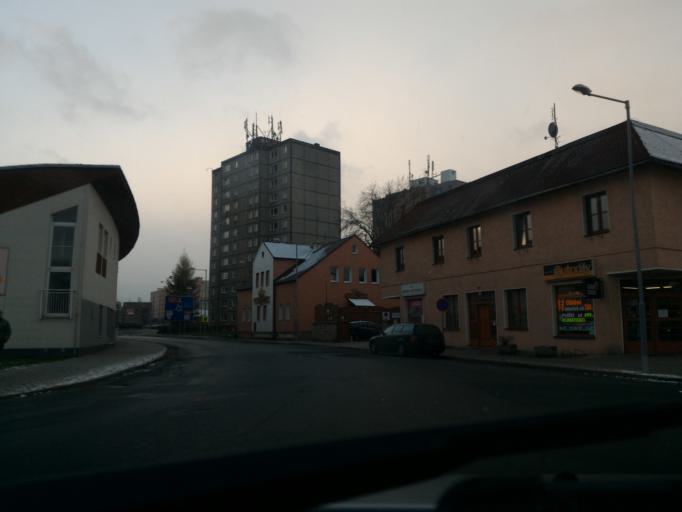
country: CZ
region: Ustecky
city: Varnsdorf
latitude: 50.9096
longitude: 14.6181
